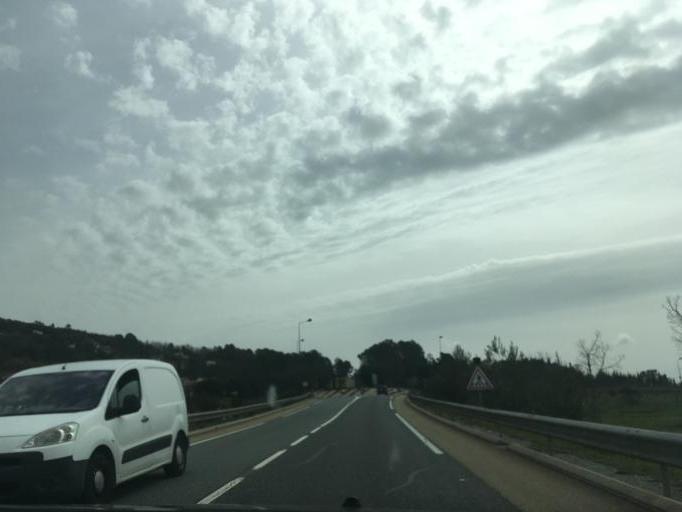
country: FR
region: Provence-Alpes-Cote d'Azur
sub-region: Departement du Var
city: Montauroux
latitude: 43.5999
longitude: 6.7841
